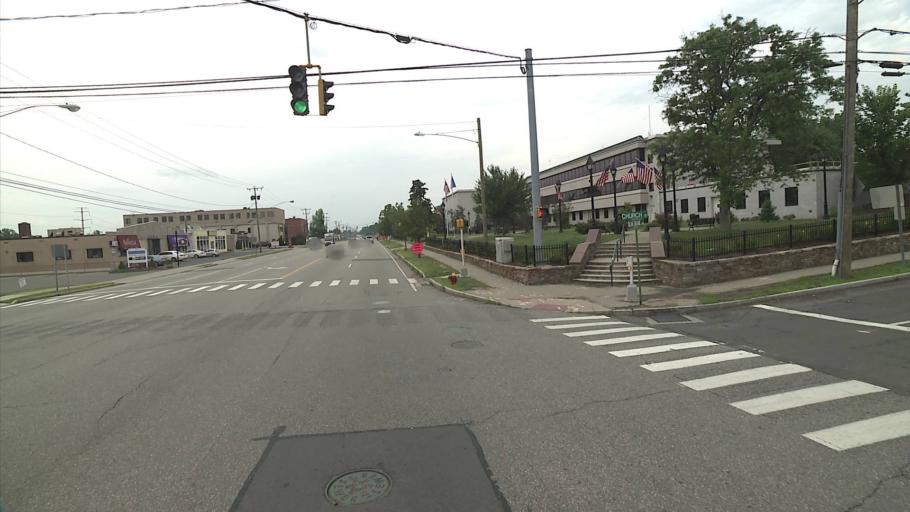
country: US
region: Connecticut
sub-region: Hartford County
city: Wethersfield
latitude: 41.7125
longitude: -72.6637
